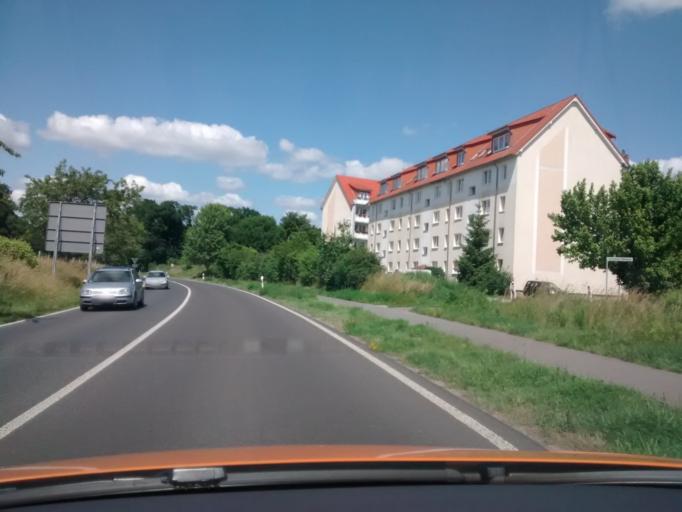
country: DE
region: Berlin
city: Kladow
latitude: 52.4719
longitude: 13.1024
